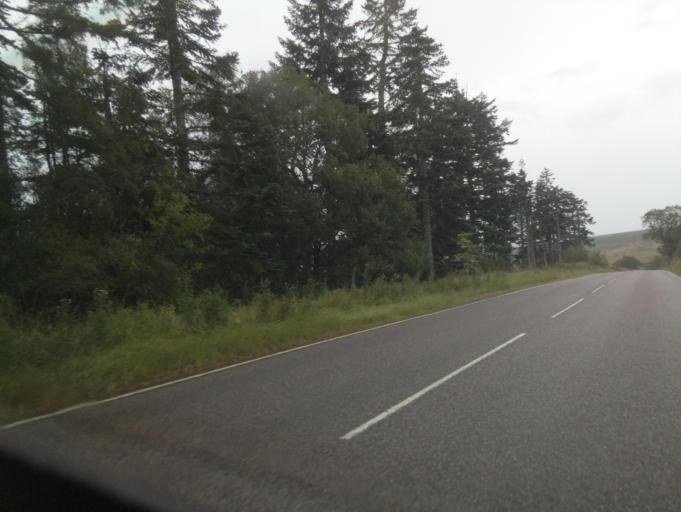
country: GB
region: Scotland
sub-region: Highland
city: Grantown on Spey
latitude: 57.2400
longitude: -3.3538
